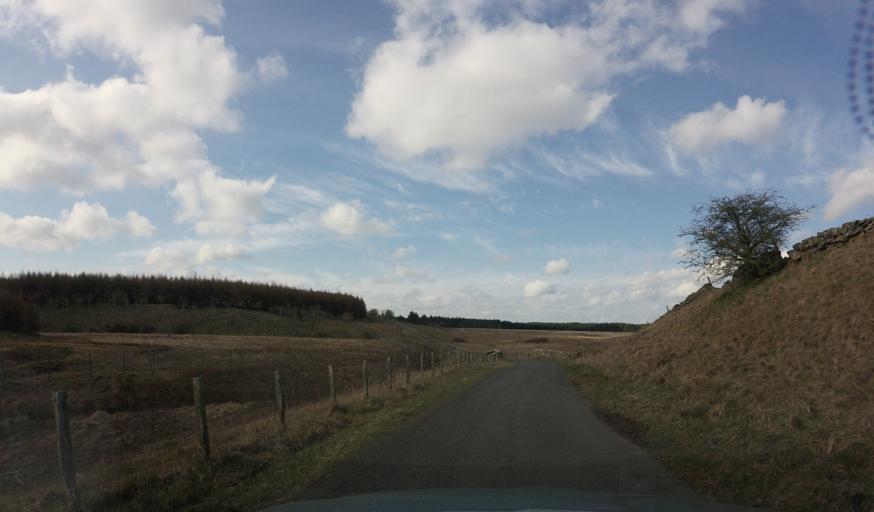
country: GB
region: Scotland
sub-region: Midlothian
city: Penicuik
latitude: 55.7857
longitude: -3.1720
